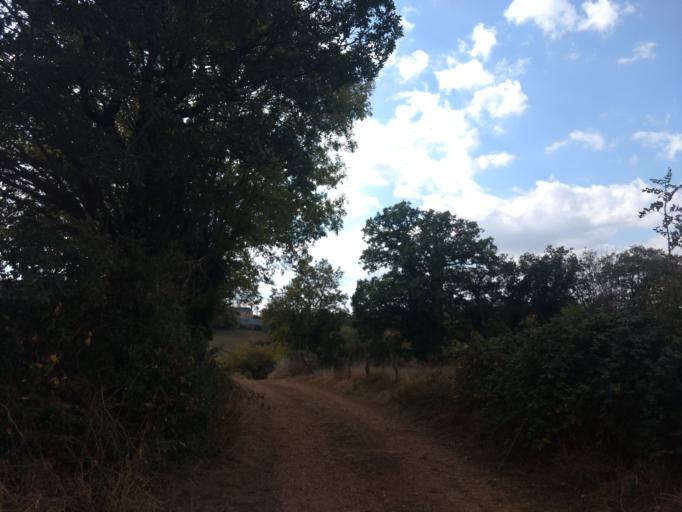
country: FR
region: Midi-Pyrenees
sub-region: Departement de l'Aveyron
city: Bozouls
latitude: 44.4689
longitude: 2.6912
